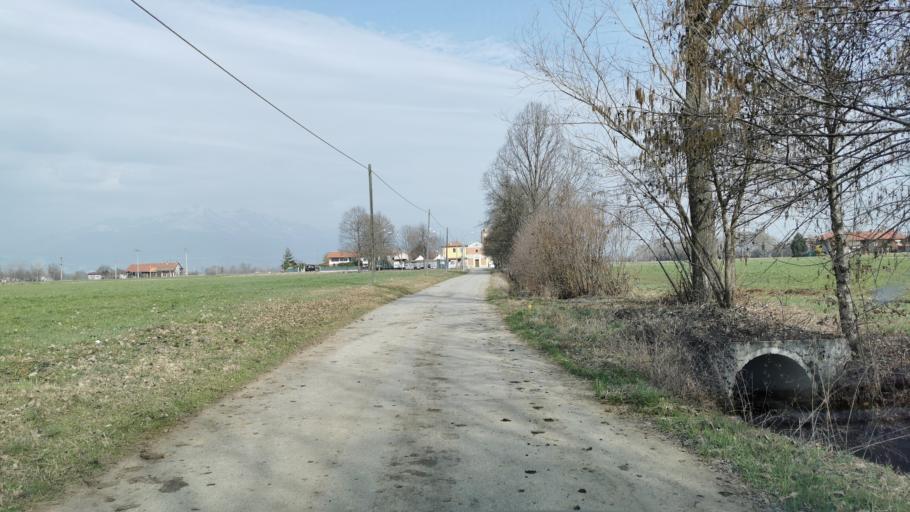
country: IT
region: Piedmont
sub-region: Provincia di Torino
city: Front
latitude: 45.2875
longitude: 7.6947
